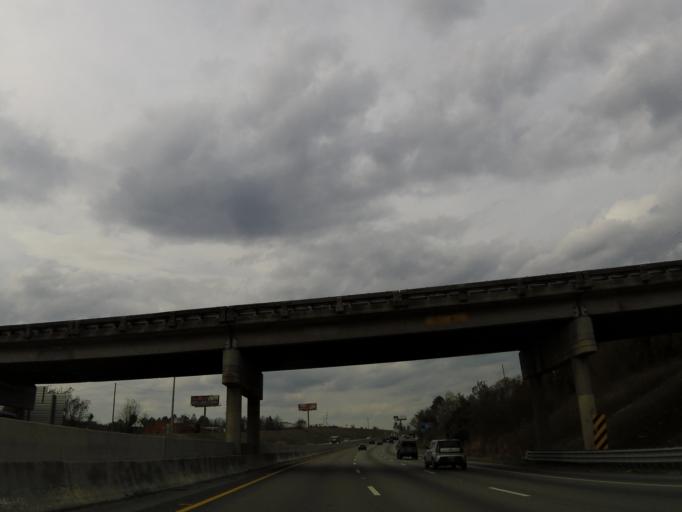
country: US
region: South Carolina
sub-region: Lexington County
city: Cayce
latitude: 33.9383
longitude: -81.0860
